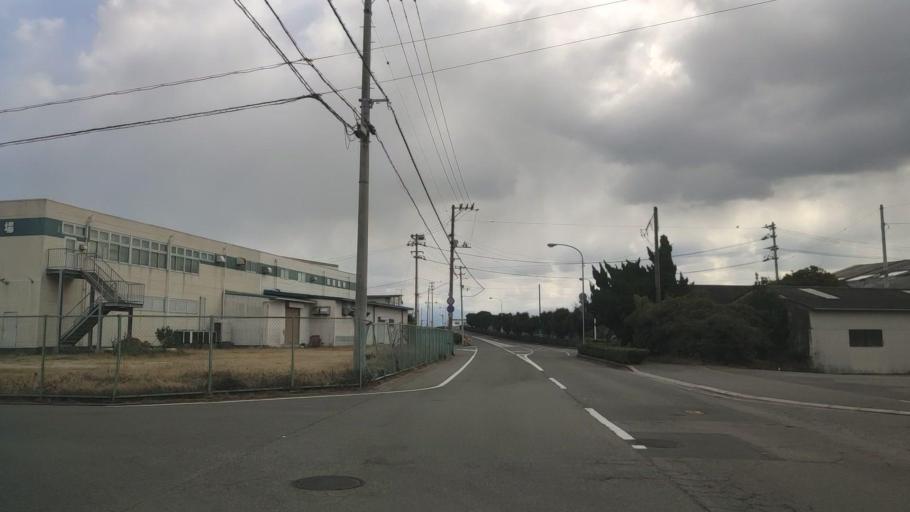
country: JP
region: Ehime
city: Saijo
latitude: 34.0534
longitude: 133.0225
